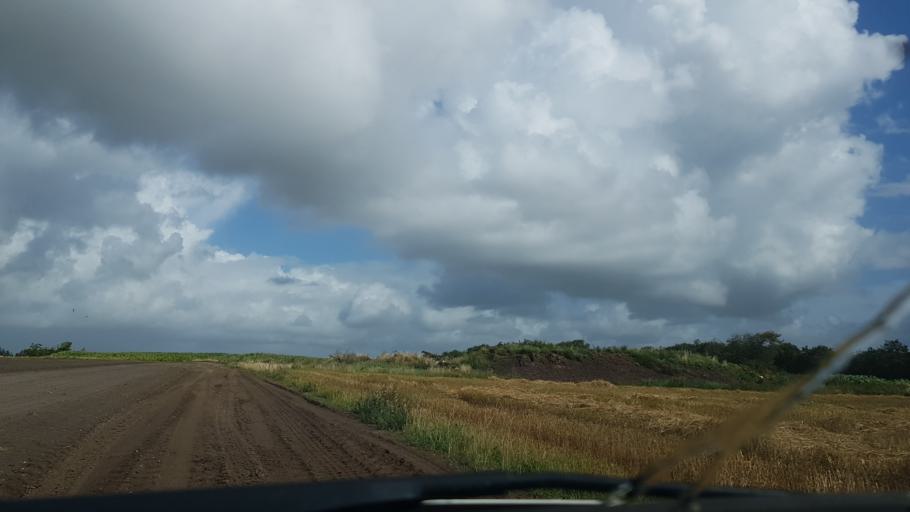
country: DK
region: South Denmark
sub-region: Esbjerg Kommune
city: Ribe
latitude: 55.2570
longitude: 8.7610
